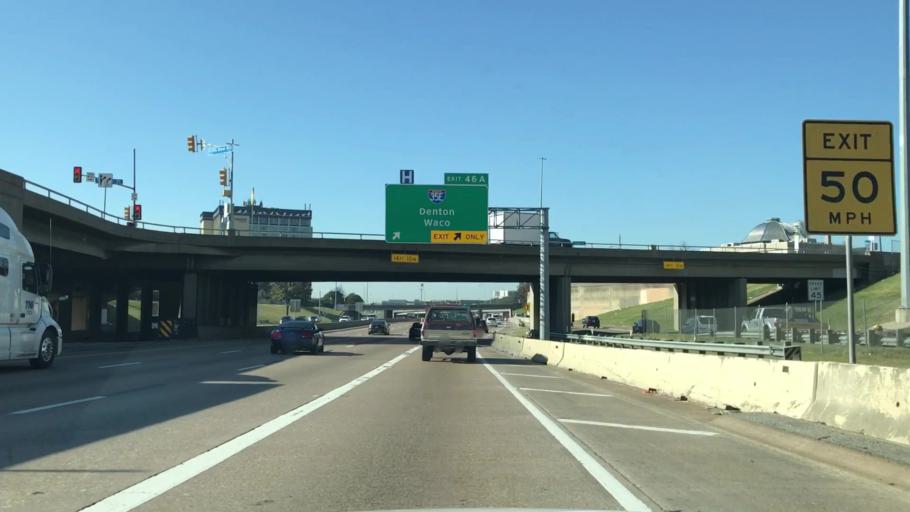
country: US
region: Texas
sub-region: Dallas County
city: Dallas
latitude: 32.7744
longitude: -96.7922
